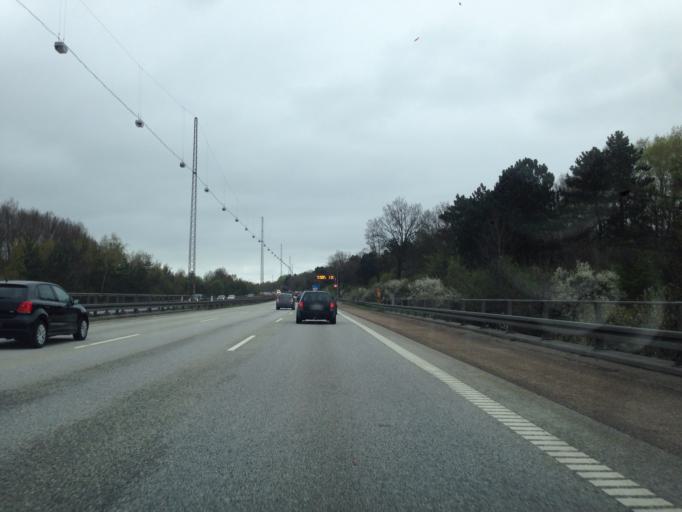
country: DK
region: Capital Region
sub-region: Rudersdal Kommune
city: Trorod
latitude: 55.8028
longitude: 12.5335
